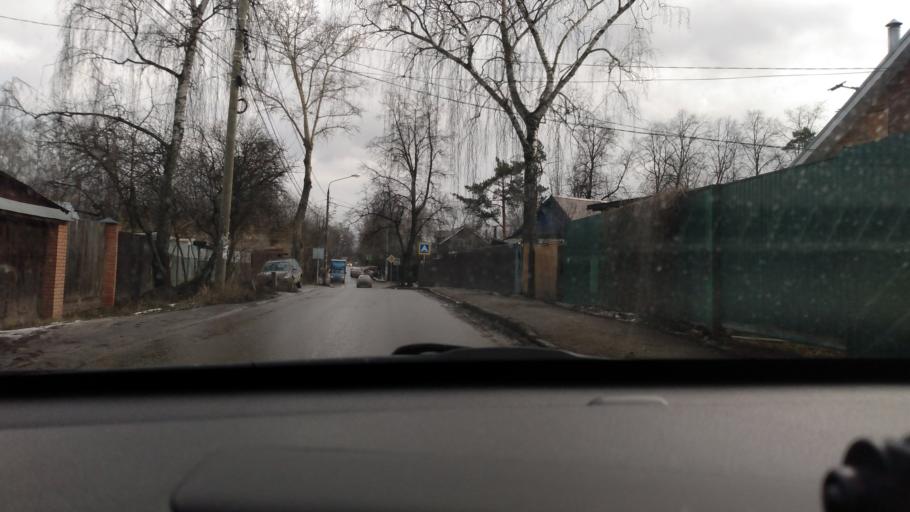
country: RU
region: Moskovskaya
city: Yubileyny
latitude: 55.9292
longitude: 37.8638
